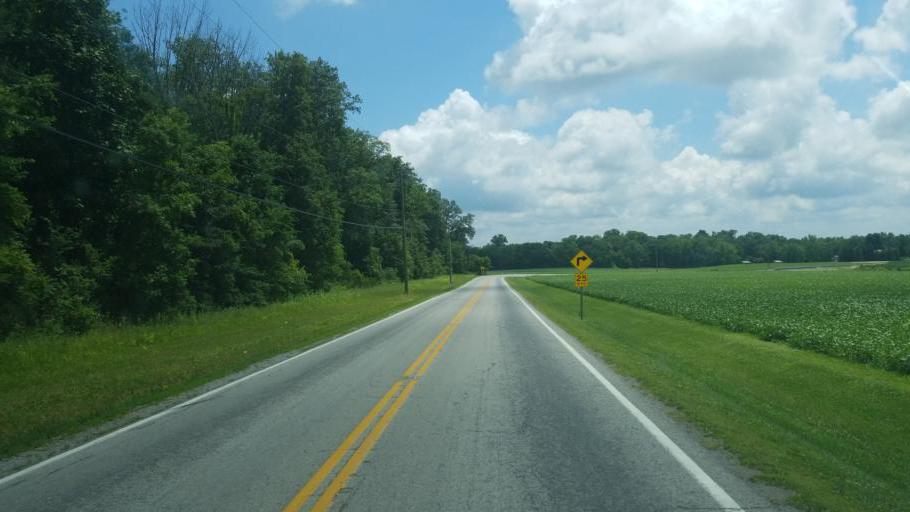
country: US
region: Ohio
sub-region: Highland County
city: Greenfield
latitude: 39.2436
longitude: -83.4353
